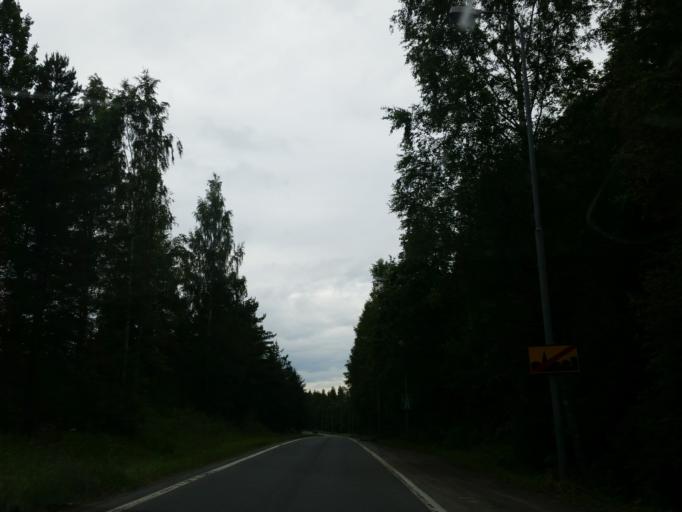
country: FI
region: Northern Savo
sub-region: Kuopio
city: Kuopio
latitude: 62.9061
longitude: 27.6874
